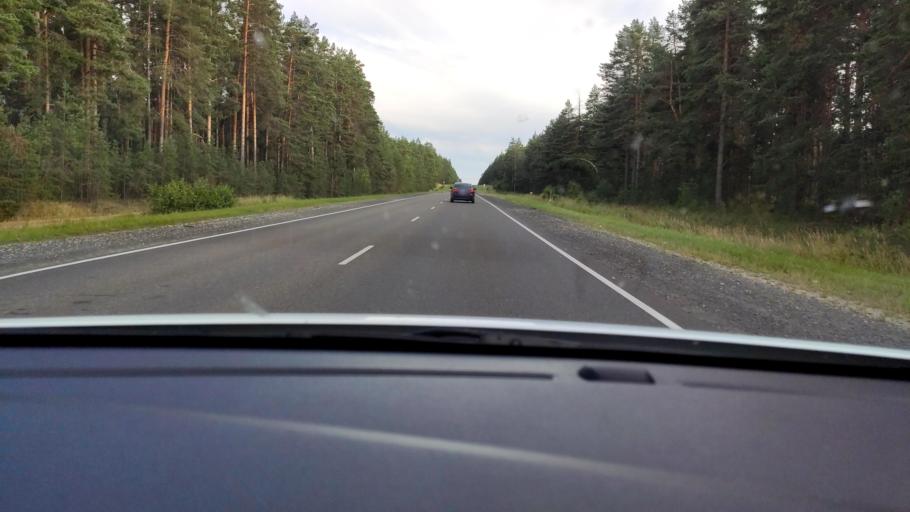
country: RU
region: Mariy-El
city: Suslonger
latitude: 56.3706
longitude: 48.2107
